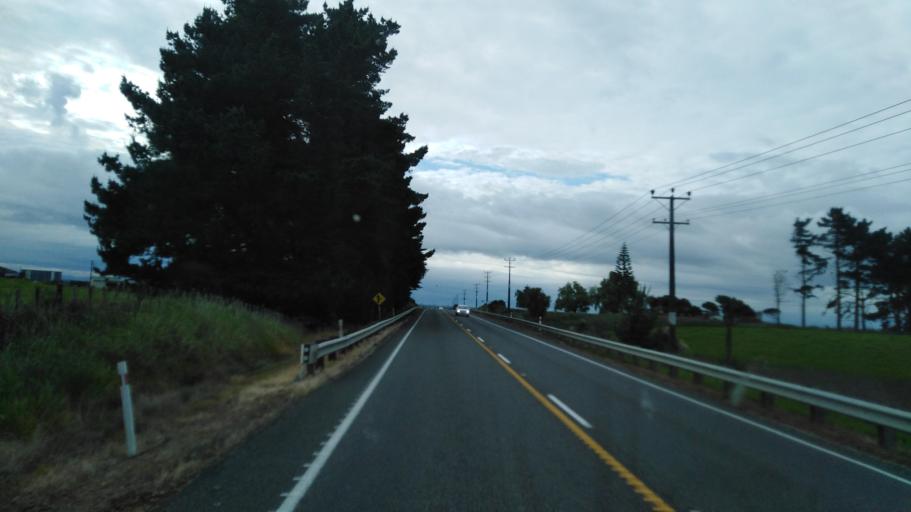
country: NZ
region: Manawatu-Wanganui
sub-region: Rangitikei District
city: Bulls
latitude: -40.1398
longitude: 175.3664
